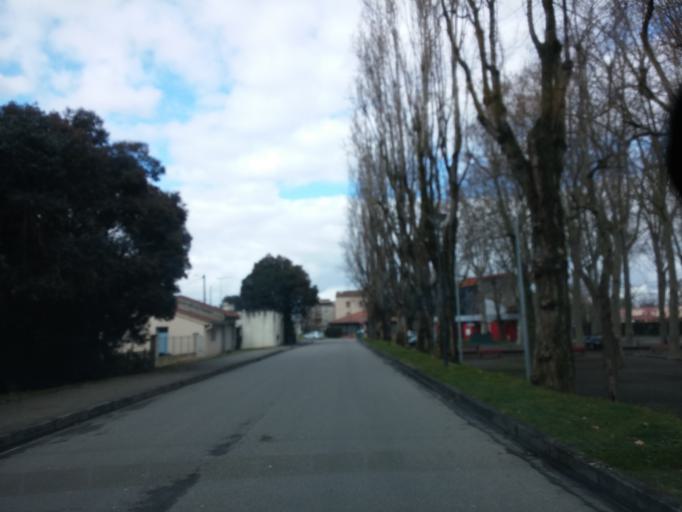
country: FR
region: Midi-Pyrenees
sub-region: Departement de la Haute-Garonne
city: Blagnac
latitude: 43.6353
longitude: 1.4006
